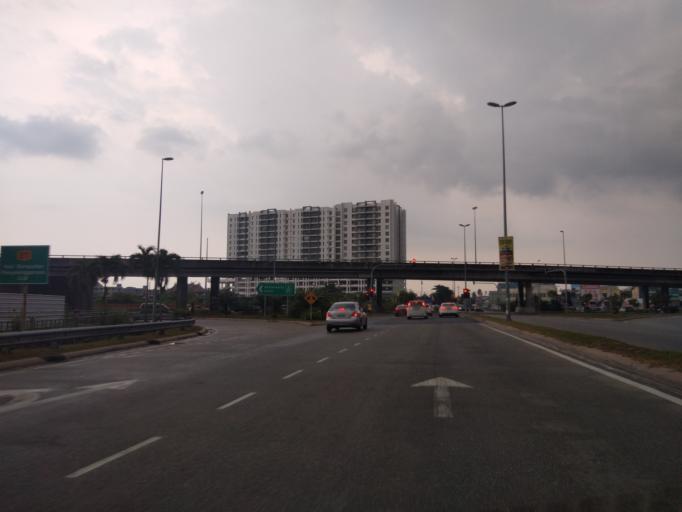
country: MY
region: Penang
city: Permatang Kuching
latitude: 5.4417
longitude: 100.3815
